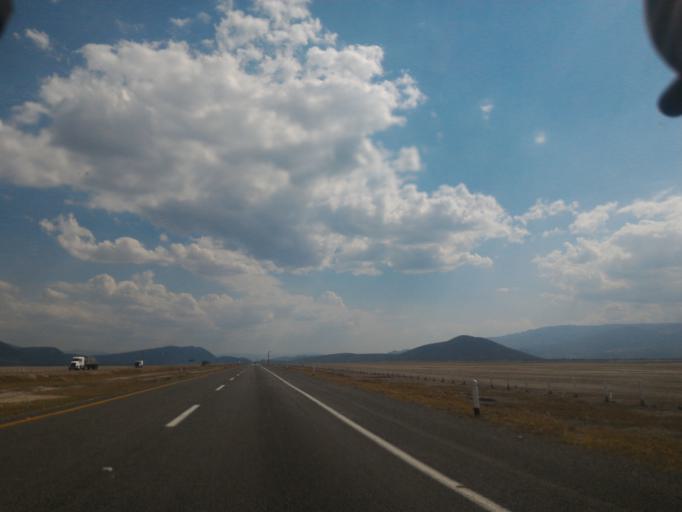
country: MX
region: Jalisco
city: Zacoalco de Torres
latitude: 20.3083
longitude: -103.5614
